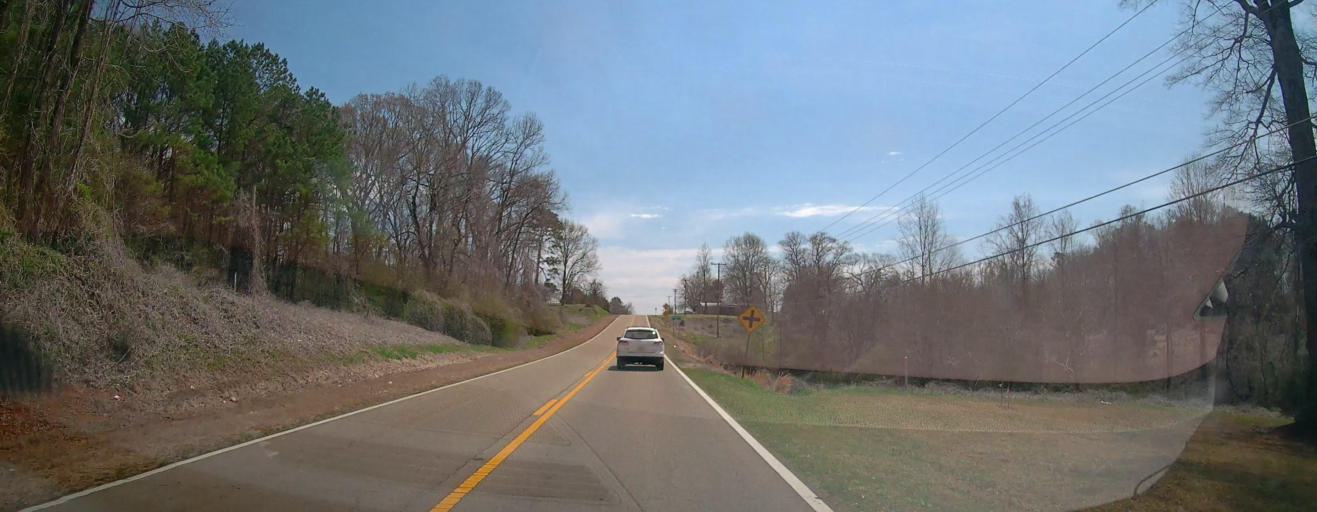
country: US
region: Mississippi
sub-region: Union County
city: New Albany
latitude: 34.4385
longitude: -88.9590
